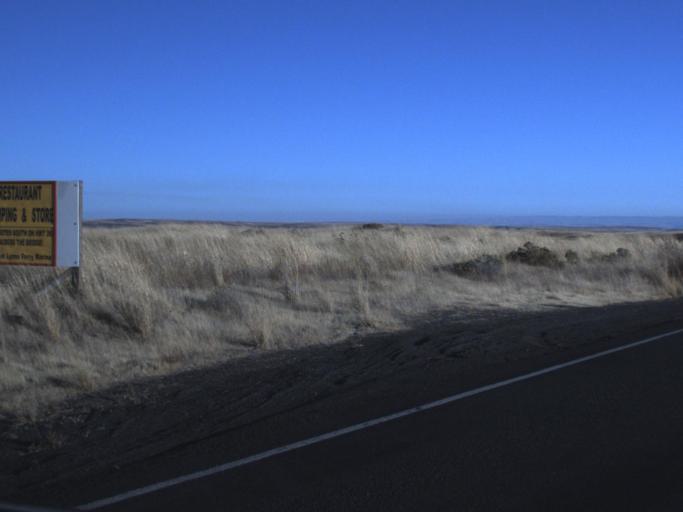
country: US
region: Washington
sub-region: Walla Walla County
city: Waitsburg
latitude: 46.6474
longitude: -118.2545
